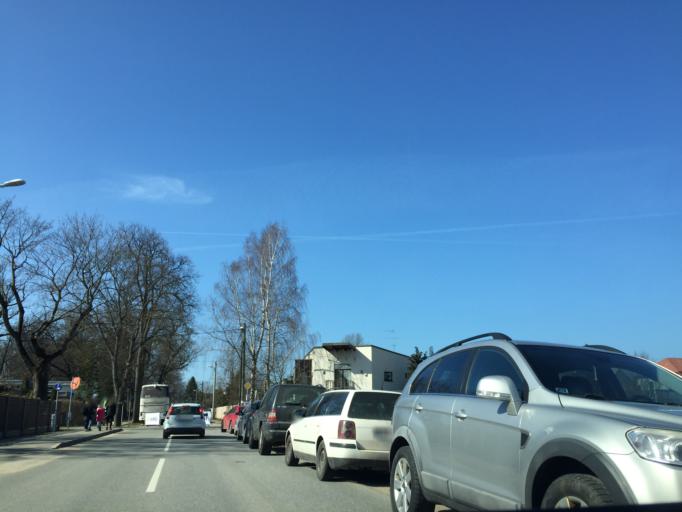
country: LV
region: Carnikava
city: Carnikava
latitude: 57.1308
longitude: 24.2783
